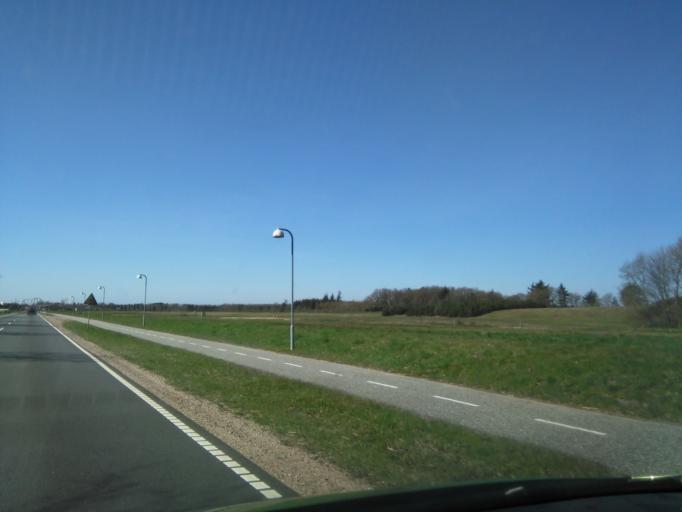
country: DK
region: South Denmark
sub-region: Billund Kommune
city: Billund
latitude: 55.7432
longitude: 9.1328
